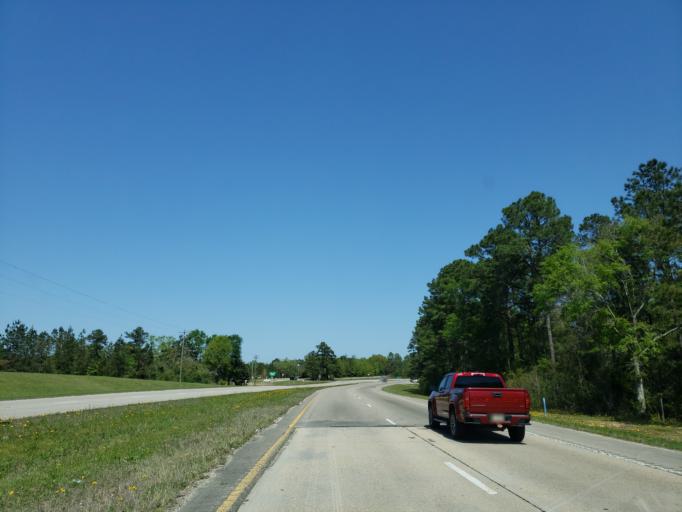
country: US
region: Mississippi
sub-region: Harrison County
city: Saucier
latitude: 30.6195
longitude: -89.1334
